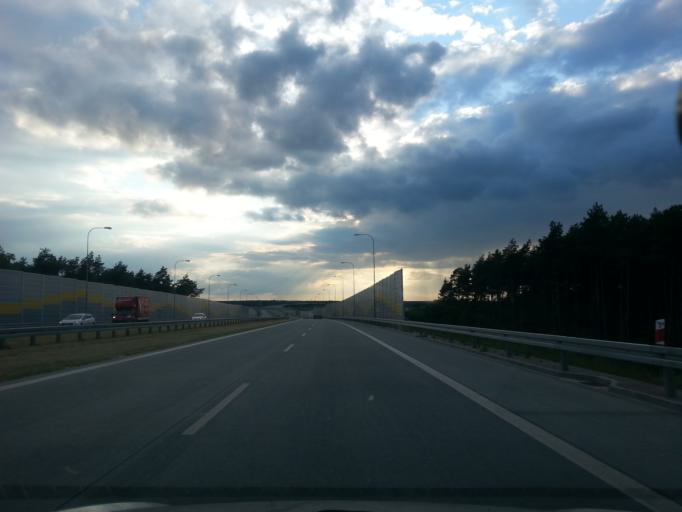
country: PL
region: Lodz Voivodeship
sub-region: Powiat zdunskowolski
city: Zdunska Wola
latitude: 51.5743
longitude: 18.9482
